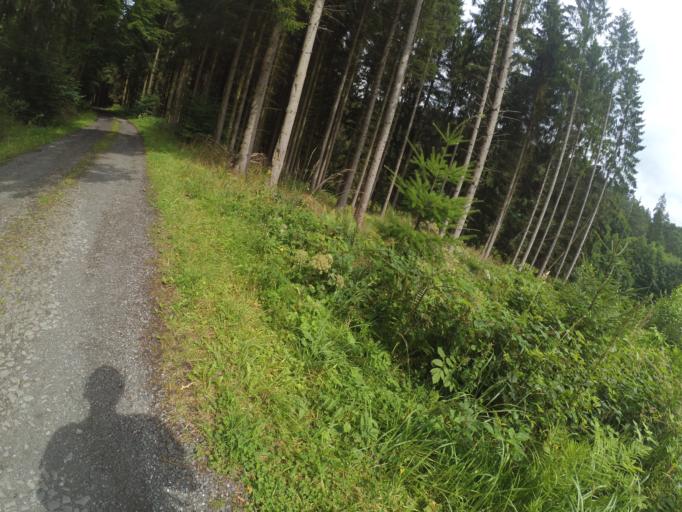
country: DE
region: Hesse
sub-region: Regierungsbezirk Kassel
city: Kirchheim
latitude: 50.8644
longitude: 9.5383
